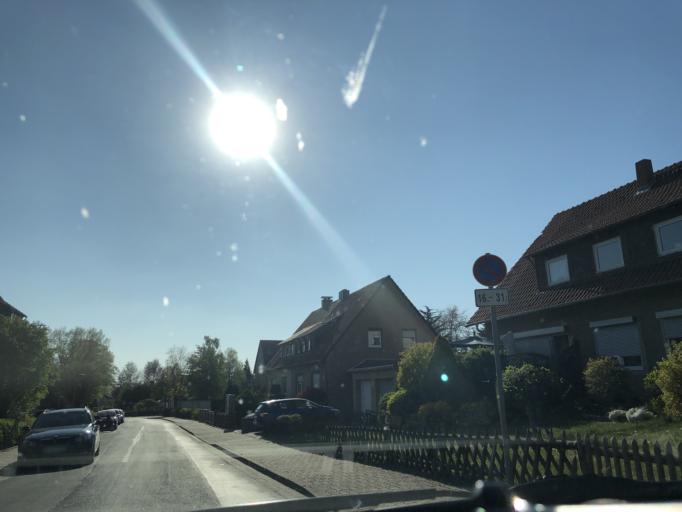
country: DE
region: Lower Saxony
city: Wolfenbuettel
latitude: 52.1706
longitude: 10.5614
